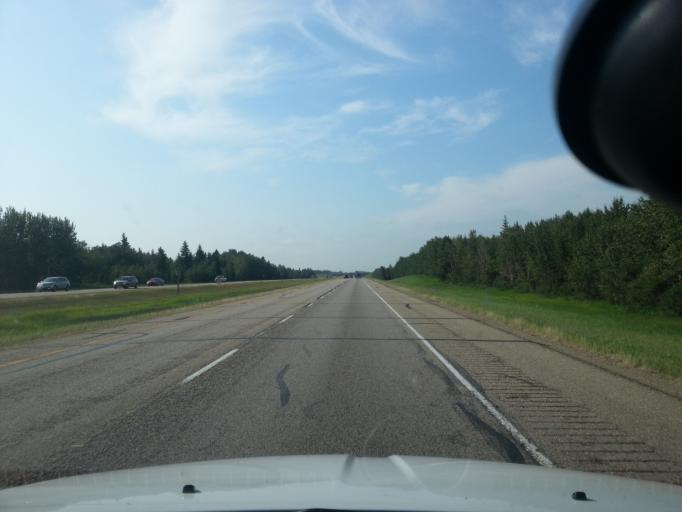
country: CA
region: Alberta
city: Lacombe
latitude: 52.5697
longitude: -113.6631
